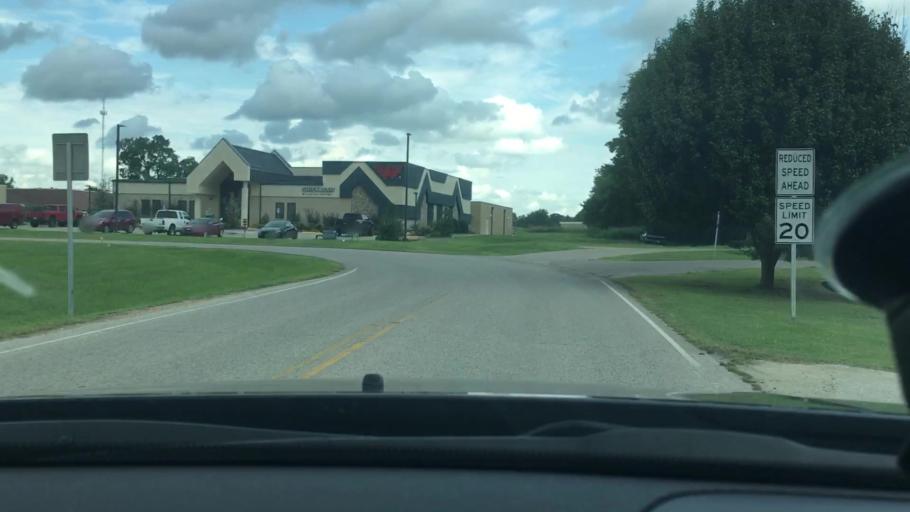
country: US
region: Oklahoma
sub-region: Johnston County
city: Tishomingo
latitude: 34.2331
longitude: -96.6626
